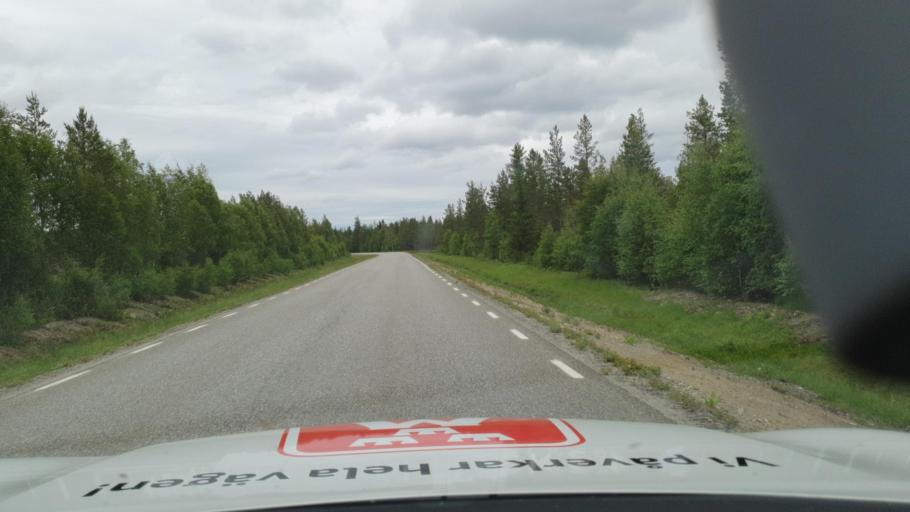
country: SE
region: Vaesterbotten
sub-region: Lycksele Kommun
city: Lycksele
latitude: 64.1851
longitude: 18.3146
